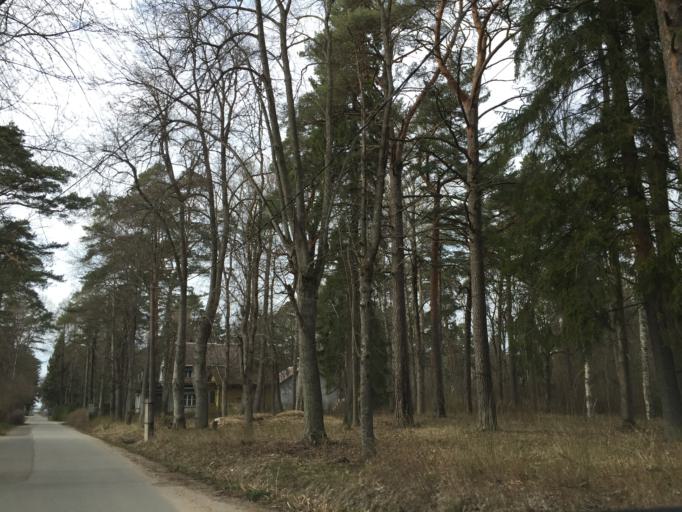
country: EE
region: Ida-Virumaa
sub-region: Narva-Joesuu linn
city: Narva-Joesuu
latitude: 59.4554
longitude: 28.0372
